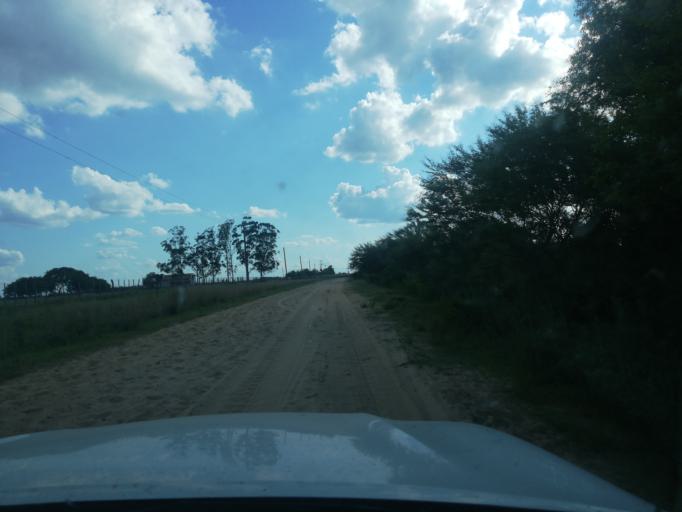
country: AR
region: Corrientes
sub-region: Departamento de San Miguel
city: San Miguel
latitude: -27.9960
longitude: -57.5790
